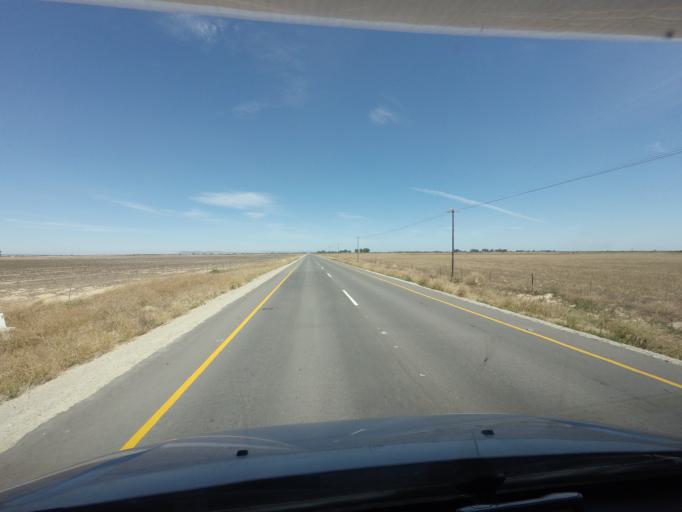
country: ZA
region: Western Cape
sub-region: West Coast District Municipality
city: Vredenburg
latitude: -32.7972
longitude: 18.2675
